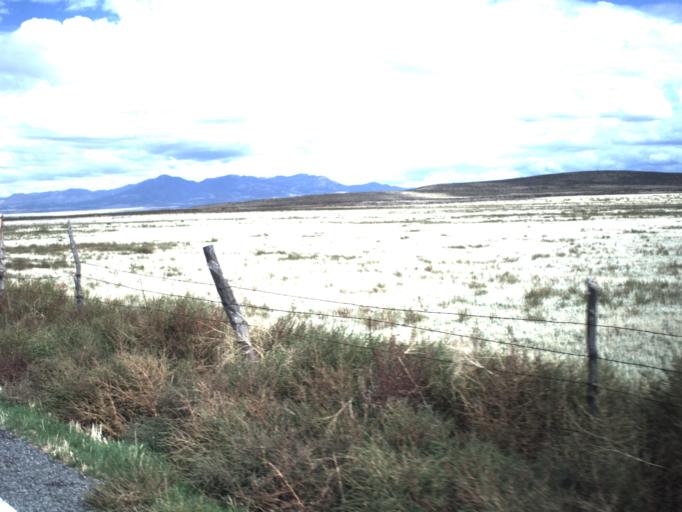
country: US
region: Utah
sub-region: Millard County
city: Fillmore
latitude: 39.0610
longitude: -112.4098
